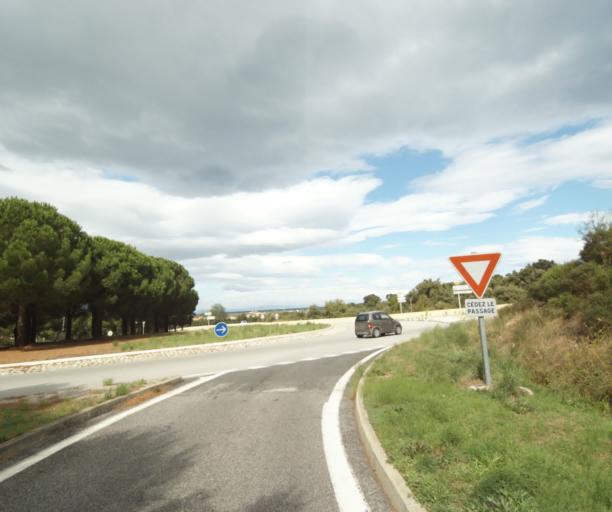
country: FR
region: Languedoc-Roussillon
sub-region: Departement des Pyrenees-Orientales
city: Collioure
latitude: 42.5314
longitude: 3.0553
